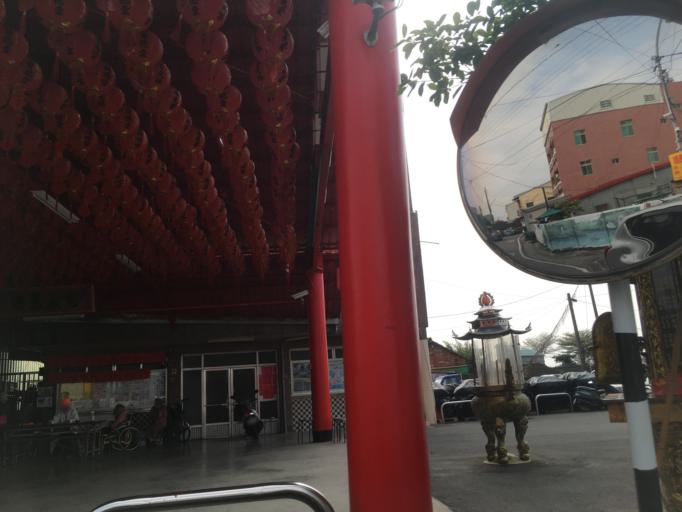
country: TW
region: Taiwan
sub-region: Yunlin
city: Douliu
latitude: 23.6898
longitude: 120.4659
